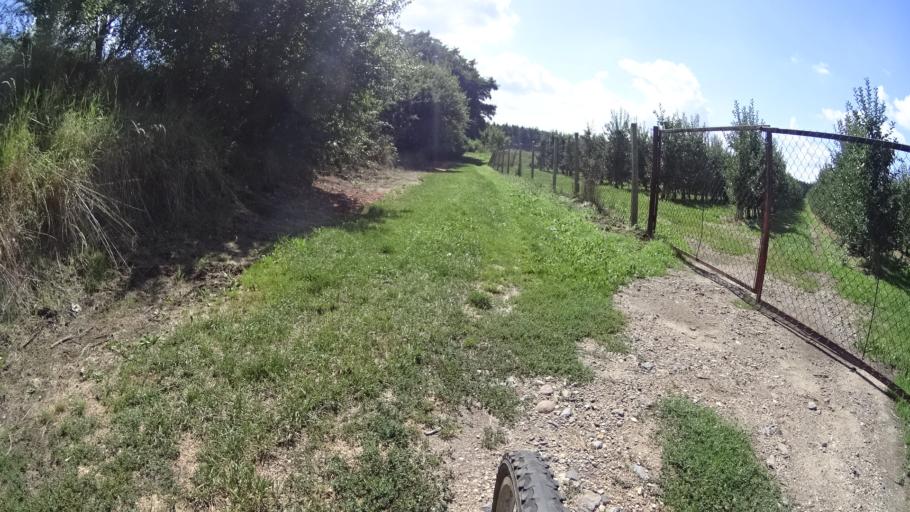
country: PL
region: Masovian Voivodeship
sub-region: Powiat grojecki
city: Mogielnica
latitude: 51.6799
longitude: 20.7521
